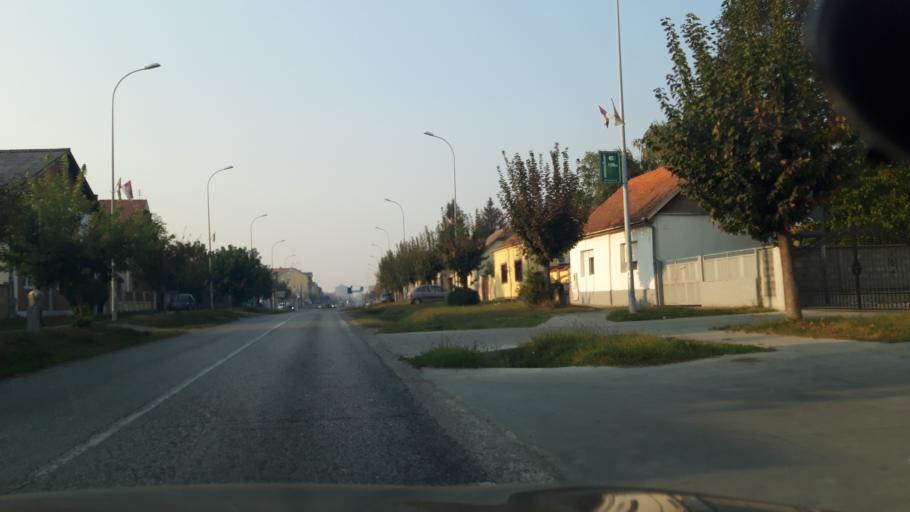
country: RS
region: Autonomna Pokrajina Vojvodina
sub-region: Sremski Okrug
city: Ingija
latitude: 45.0396
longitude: 20.0896
